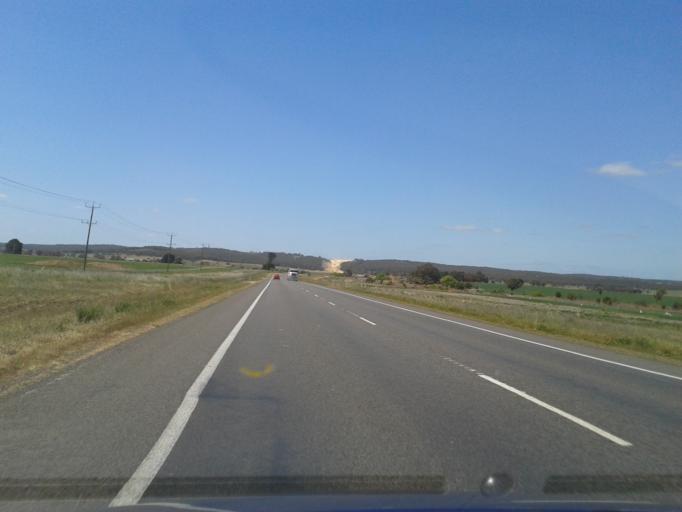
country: AU
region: Victoria
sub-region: Ararat
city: Ararat
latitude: -37.4004
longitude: 143.2932
